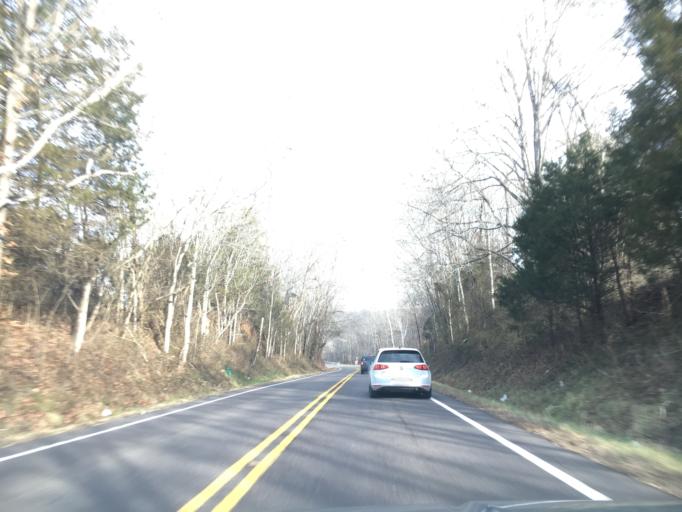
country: US
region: Virginia
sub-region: Culpeper County
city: Culpeper
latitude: 38.5877
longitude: -77.9704
